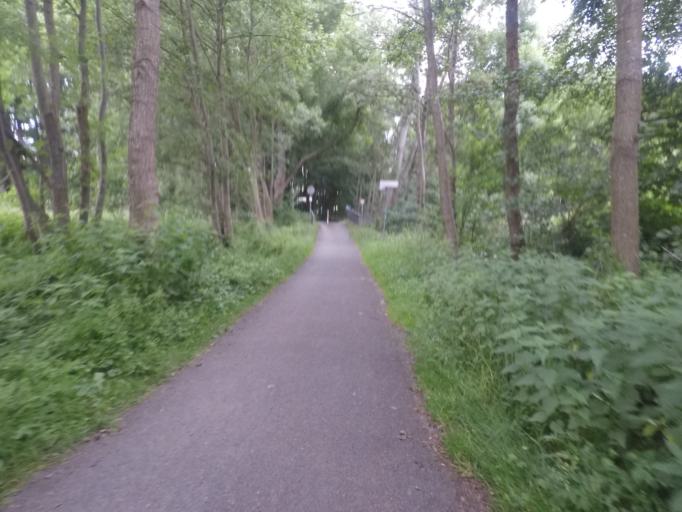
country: DE
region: North Rhine-Westphalia
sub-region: Regierungsbezirk Detmold
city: Hiddenhausen
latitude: 52.1636
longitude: 8.6006
